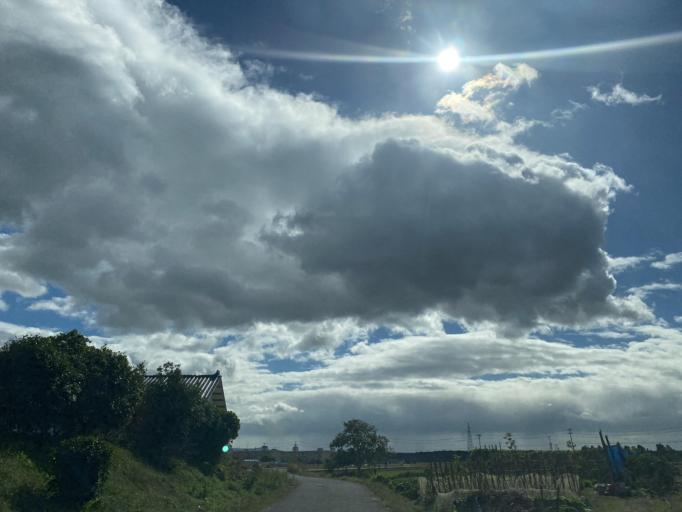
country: JP
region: Fukushima
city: Koriyama
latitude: 37.3763
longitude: 140.3314
